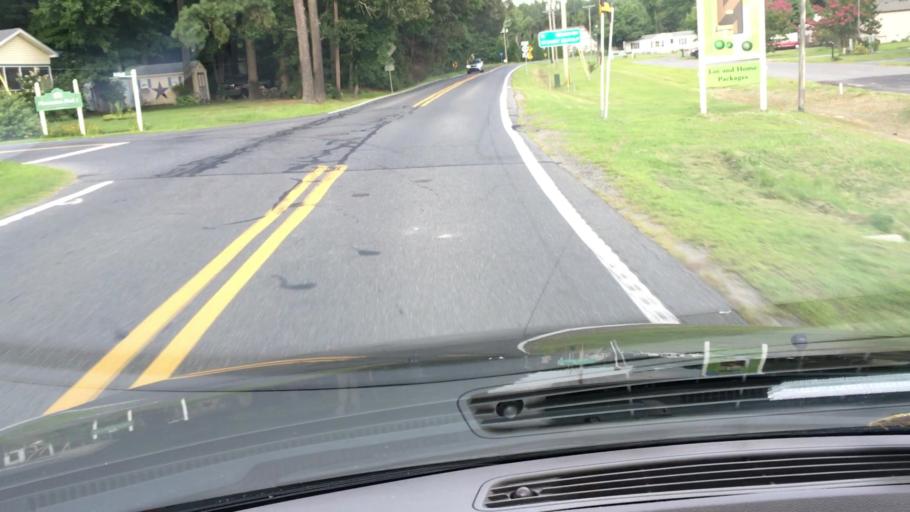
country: US
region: Delaware
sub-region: Sussex County
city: Ocean View
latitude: 38.5129
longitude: -75.1069
